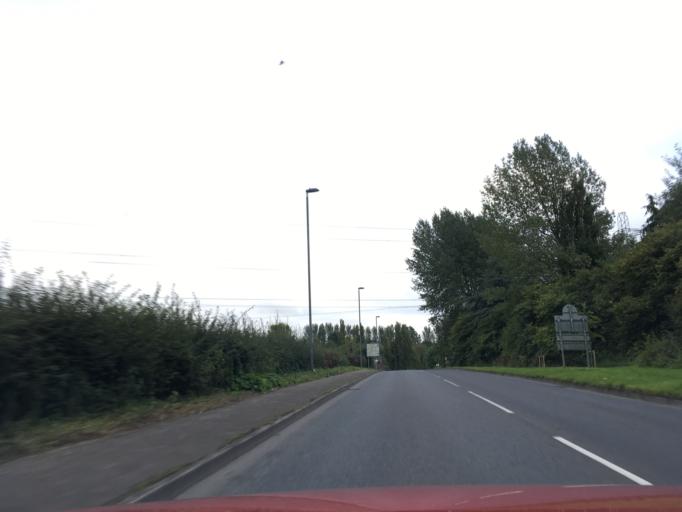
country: GB
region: England
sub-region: South Gloucestershire
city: Thornbury
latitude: 51.6013
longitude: -2.5035
